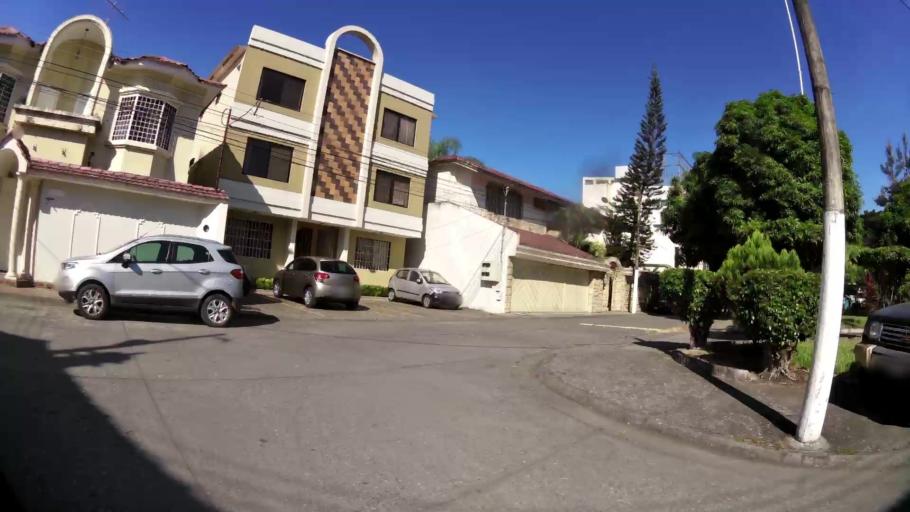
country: EC
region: Guayas
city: Eloy Alfaro
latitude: -2.1541
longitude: -79.9001
